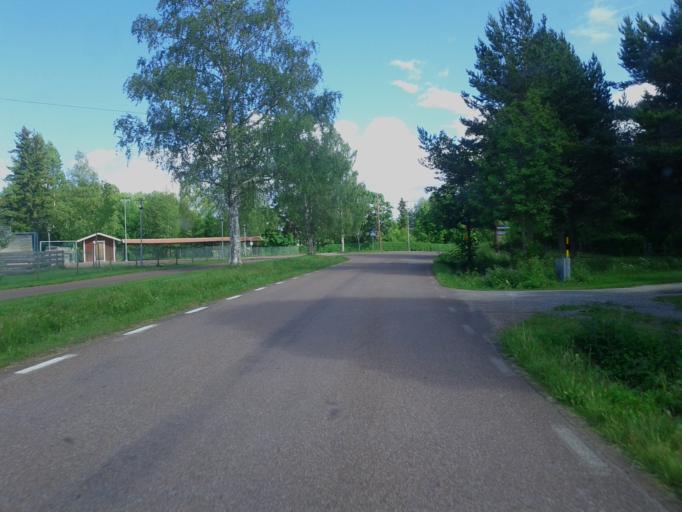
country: SE
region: Dalarna
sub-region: Rattviks Kommun
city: Raettvik
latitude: 60.9172
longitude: 15.0924
